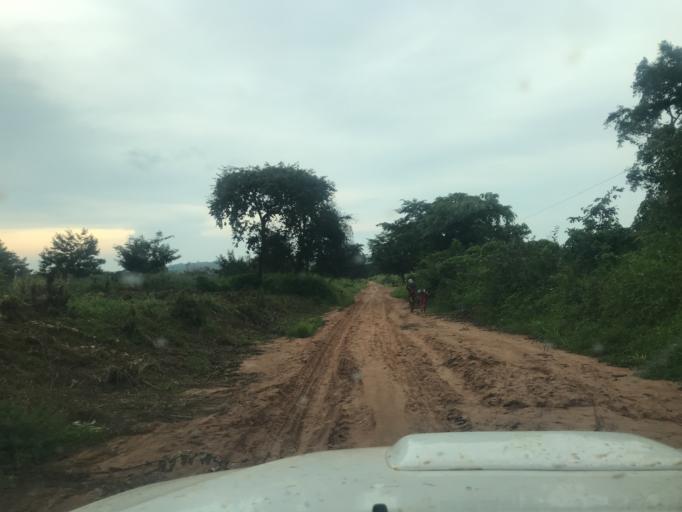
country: TZ
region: Mtwara
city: Newala Kisimani
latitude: -11.3778
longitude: 39.3500
